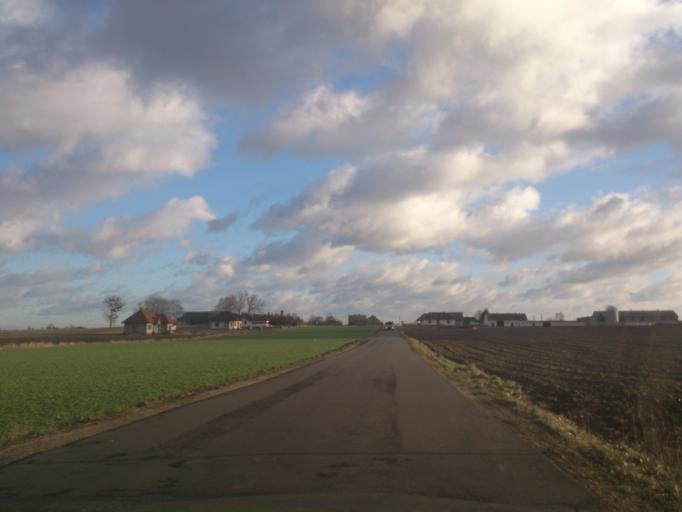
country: PL
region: Kujawsko-Pomorskie
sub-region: Powiat torunski
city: Obrowo
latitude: 53.0234
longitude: 18.8578
